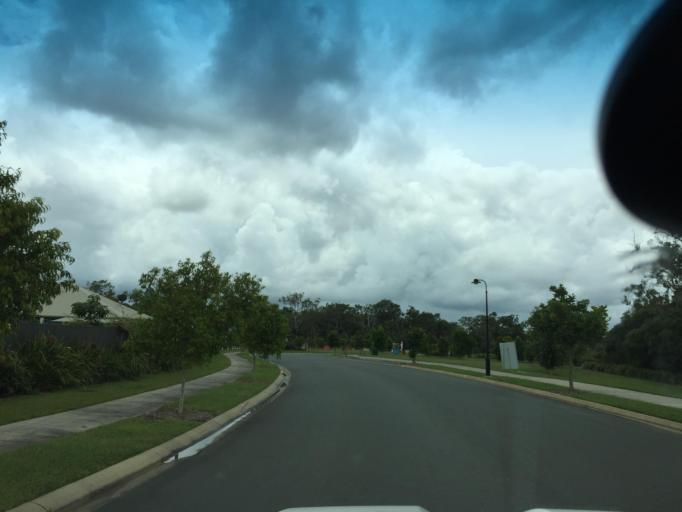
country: AU
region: Queensland
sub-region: Moreton Bay
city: Caboolture
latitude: -27.0616
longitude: 152.9300
